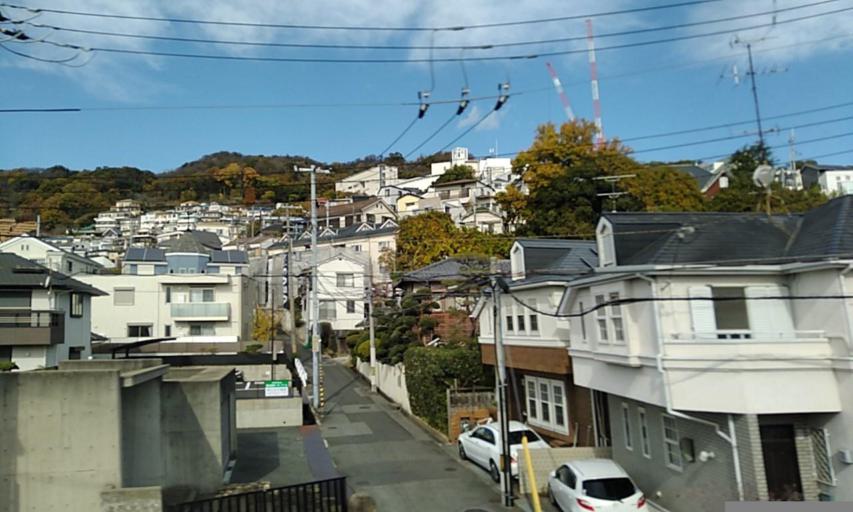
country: JP
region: Hyogo
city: Ashiya
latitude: 34.7300
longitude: 135.2835
